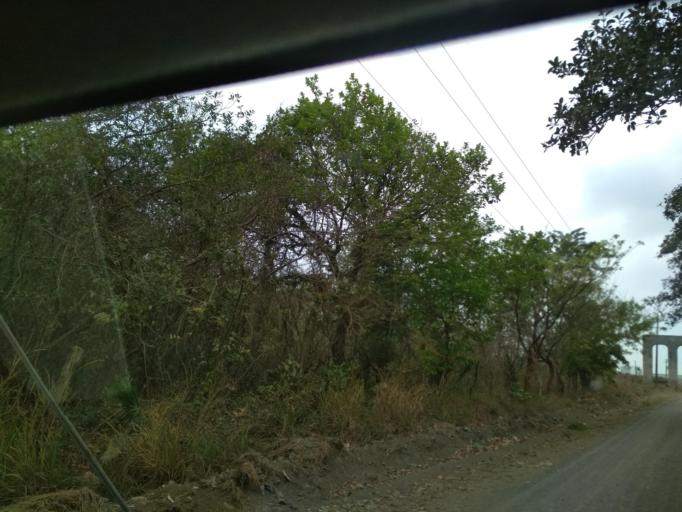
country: MX
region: Veracruz
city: Paso del Toro
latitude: 19.0188
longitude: -96.1351
